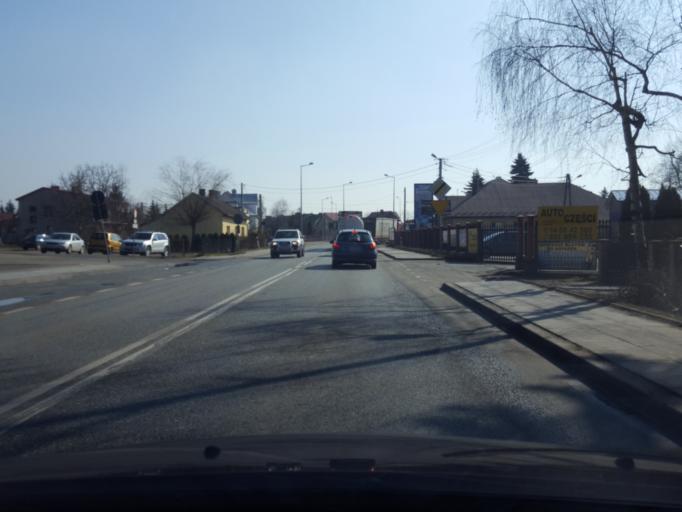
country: PL
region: Lesser Poland Voivodeship
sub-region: Powiat brzeski
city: Czchow
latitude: 49.8514
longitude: 20.6864
